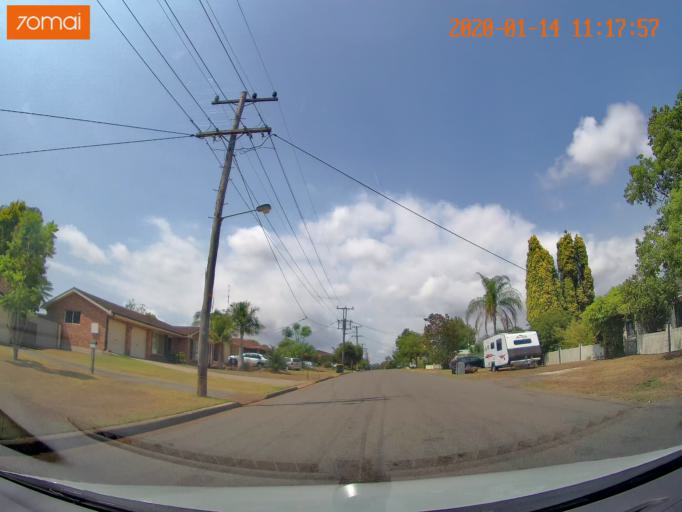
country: AU
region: New South Wales
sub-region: Lake Macquarie Shire
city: Cooranbong
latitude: -33.0944
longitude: 151.4610
